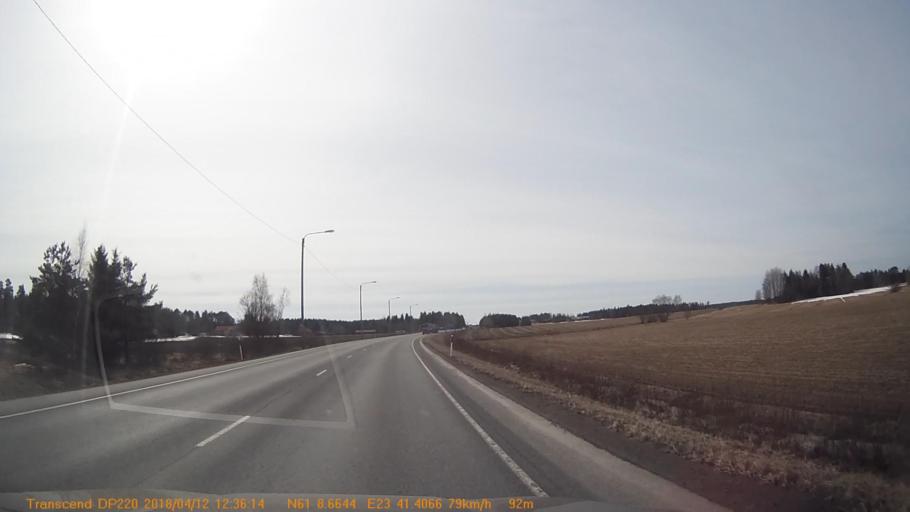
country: FI
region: Pirkanmaa
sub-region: Etelae-Pirkanmaa
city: Kylmaekoski
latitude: 61.1446
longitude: 23.6903
